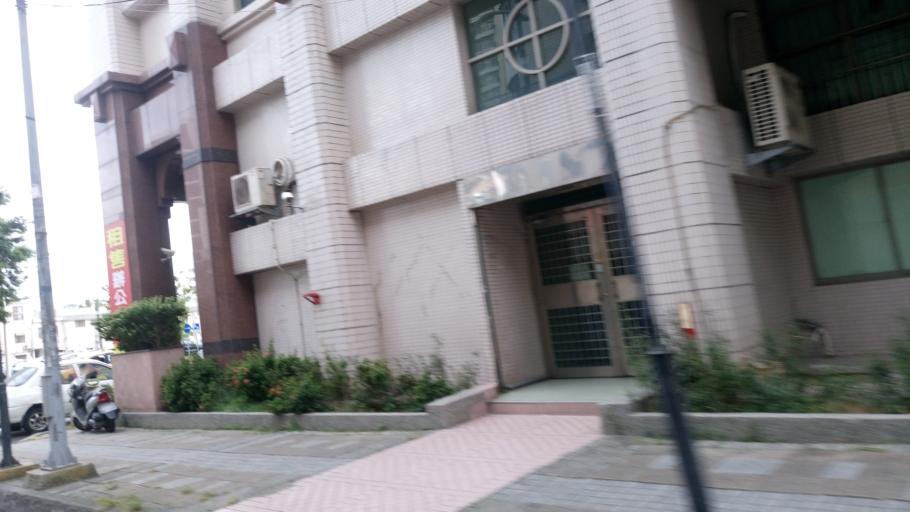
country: TW
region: Taiwan
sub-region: Hsinchu
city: Hsinchu
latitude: 24.8101
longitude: 120.9676
